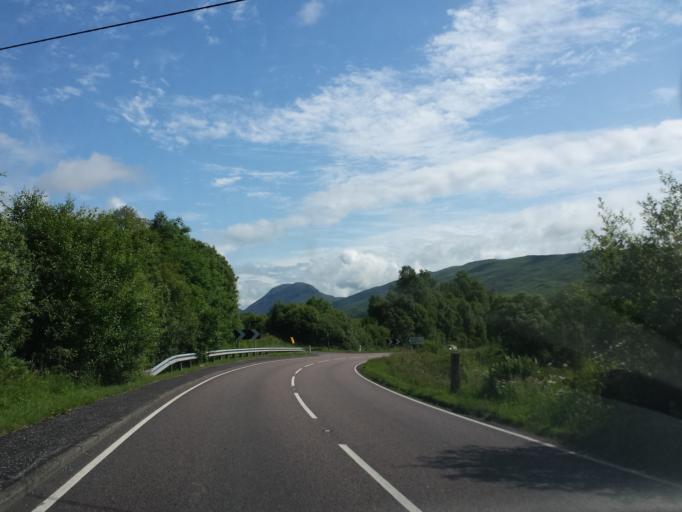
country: GB
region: Scotland
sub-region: Argyll and Bute
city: Garelochhead
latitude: 56.4100
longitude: -5.0297
